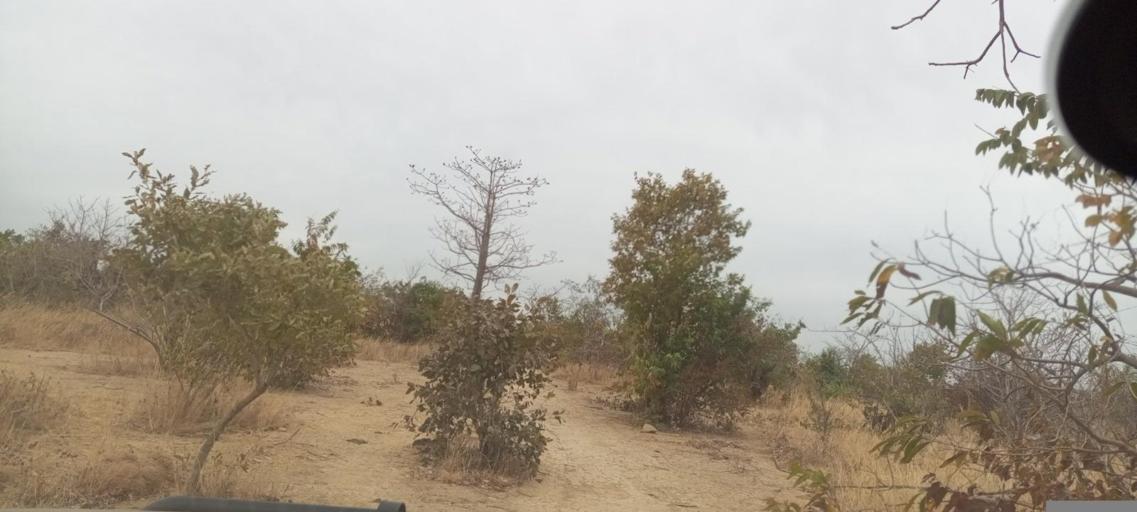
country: ML
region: Koulikoro
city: Kati
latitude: 12.7702
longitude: -8.3793
